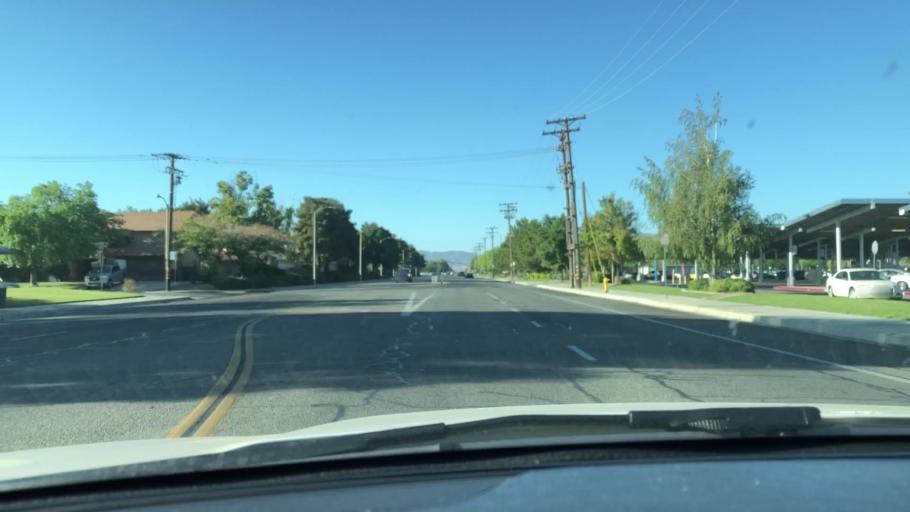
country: US
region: California
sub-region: Los Angeles County
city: Quartz Hill
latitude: 34.6791
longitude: -118.1837
